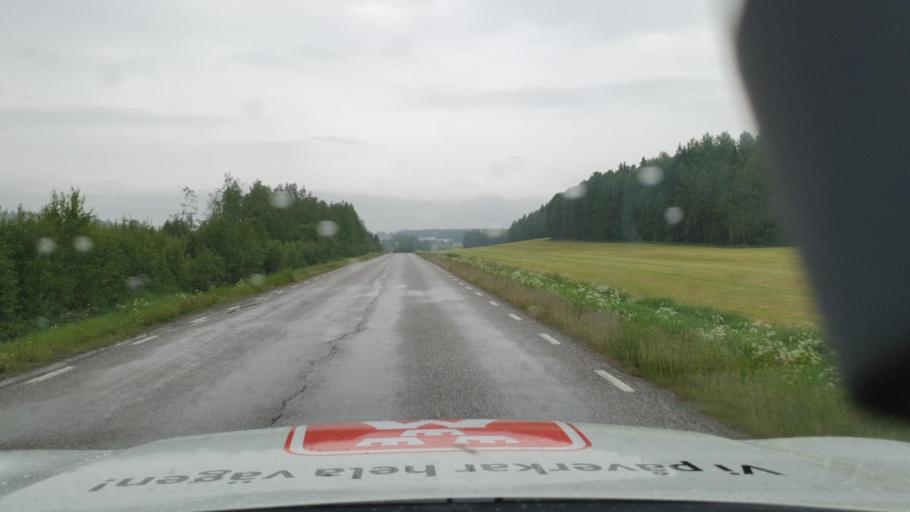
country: SE
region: Vaesterbotten
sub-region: Vannas Kommun
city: Vaennaes
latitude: 63.7857
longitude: 19.5799
